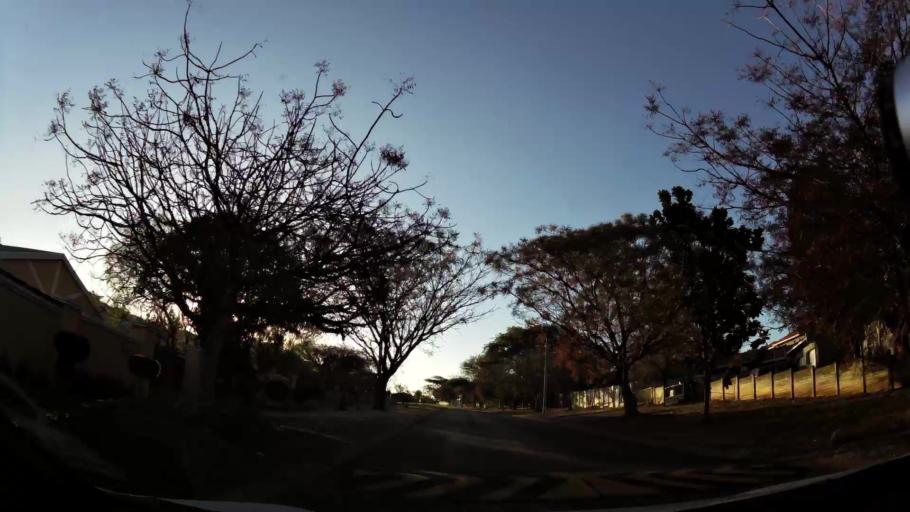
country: ZA
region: North-West
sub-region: Bojanala Platinum District Municipality
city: Rustenburg
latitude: -25.7130
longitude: 27.2367
